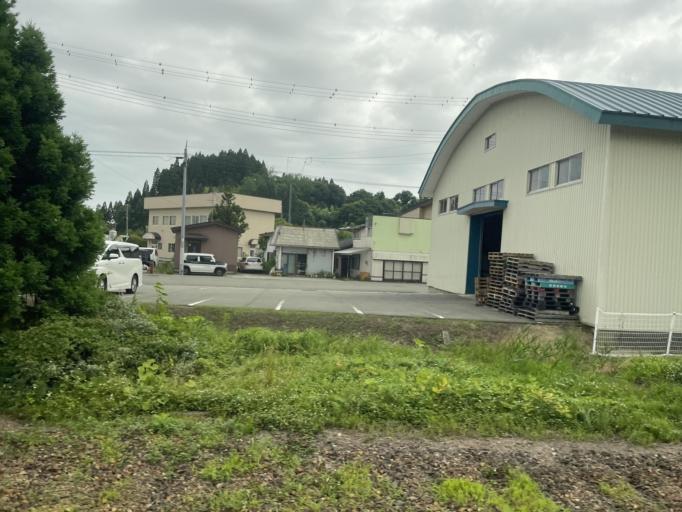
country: JP
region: Akita
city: Tenno
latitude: 39.9149
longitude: 139.9046
